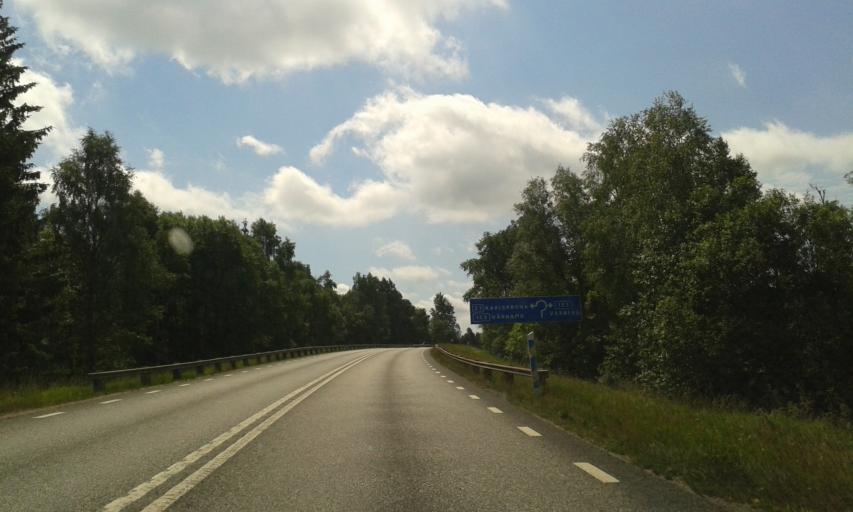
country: SE
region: Joenkoeping
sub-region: Varnamo Kommun
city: Bredaryd
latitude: 57.1742
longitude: 13.7630
